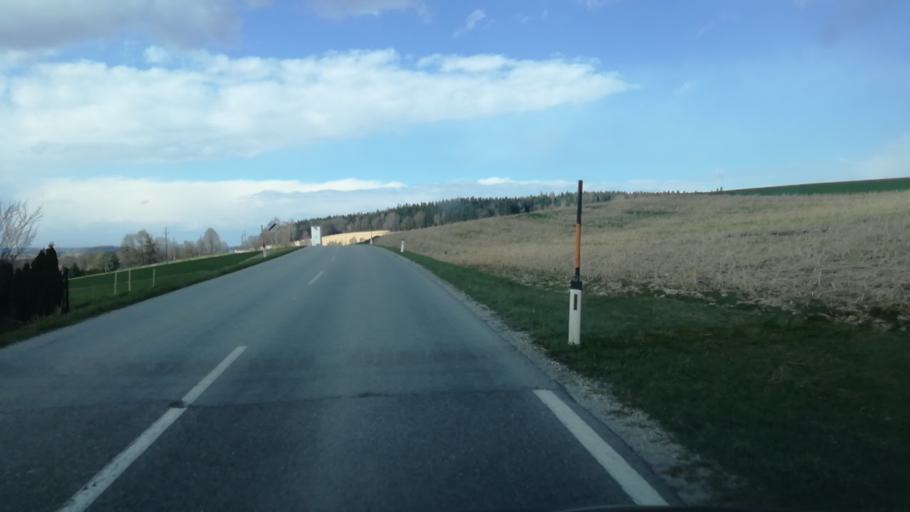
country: AT
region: Upper Austria
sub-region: Politischer Bezirk Ried im Innkreis
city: Ried im Innkreis
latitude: 48.1704
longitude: 13.4844
